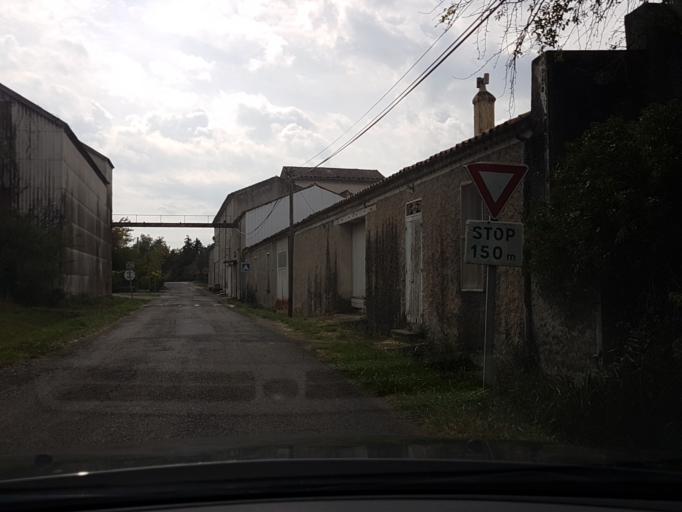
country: FR
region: Provence-Alpes-Cote d'Azur
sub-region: Departement du Vaucluse
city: Saint-Saturnin-les-Avignon
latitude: 43.9612
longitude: 4.9406
